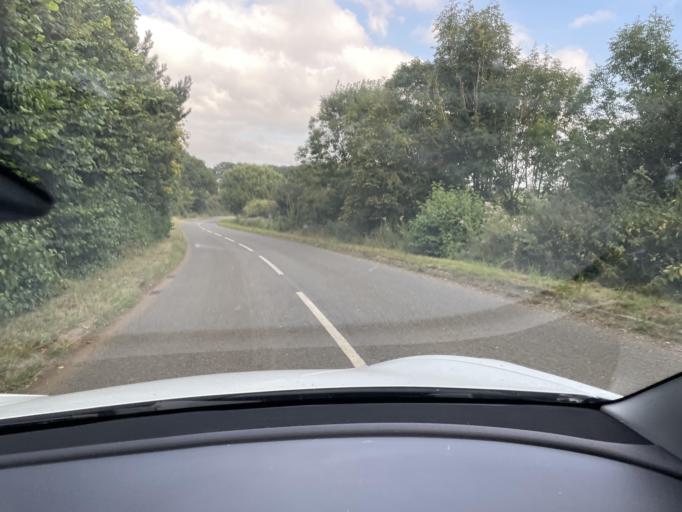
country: GB
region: England
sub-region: Leicestershire
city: Market Harborough
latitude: 52.4002
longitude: -0.9967
